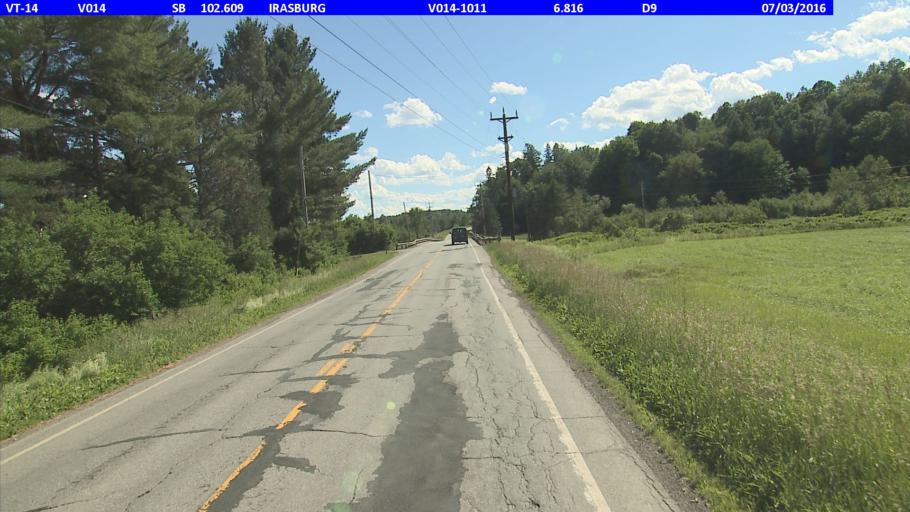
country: US
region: Vermont
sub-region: Orleans County
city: Newport
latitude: 44.8537
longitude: -72.2746
